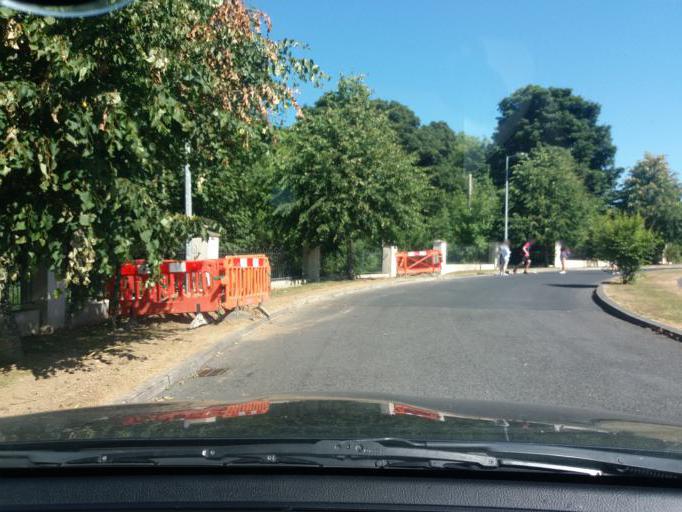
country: IE
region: Leinster
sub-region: Fingal County
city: Swords
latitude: 53.4564
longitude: -6.2588
